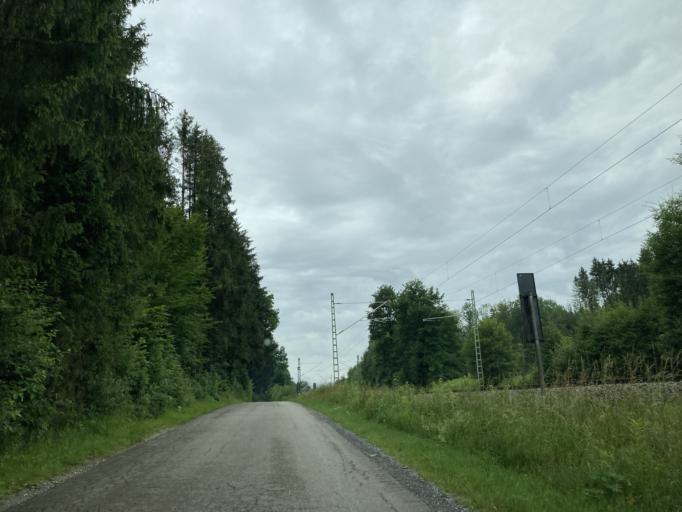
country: DE
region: Bavaria
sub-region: Upper Bavaria
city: Prutting
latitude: 47.8681
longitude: 12.2186
